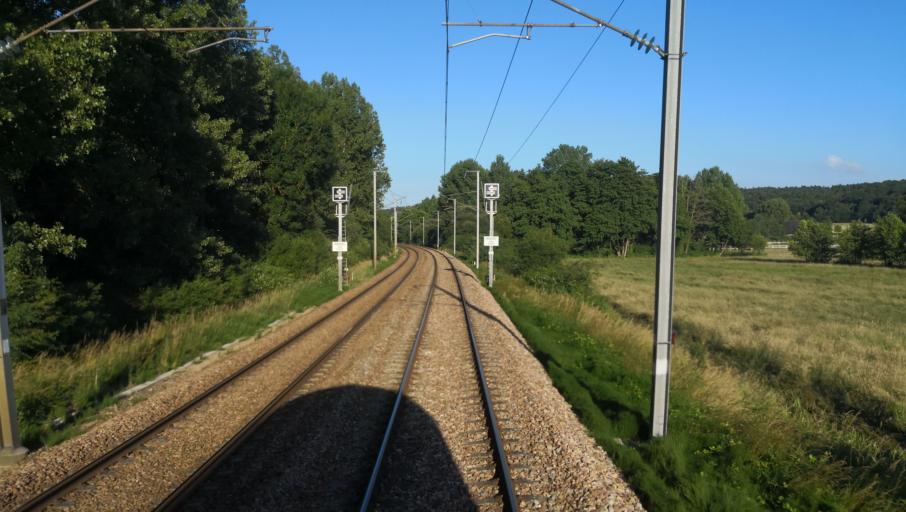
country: FR
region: Haute-Normandie
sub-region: Departement de l'Eure
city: Menneval
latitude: 49.0909
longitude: 0.6486
